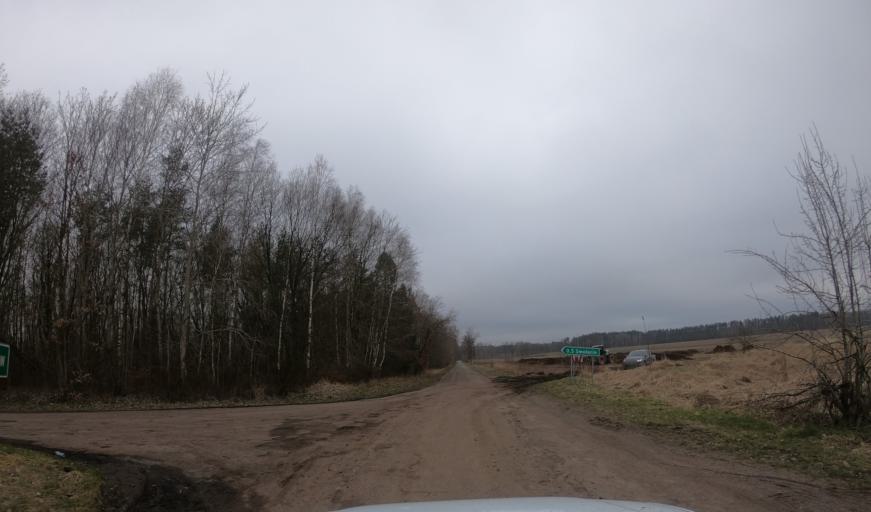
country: PL
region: West Pomeranian Voivodeship
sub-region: Powiat gryficki
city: Gryfice
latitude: 53.8806
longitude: 15.2440
